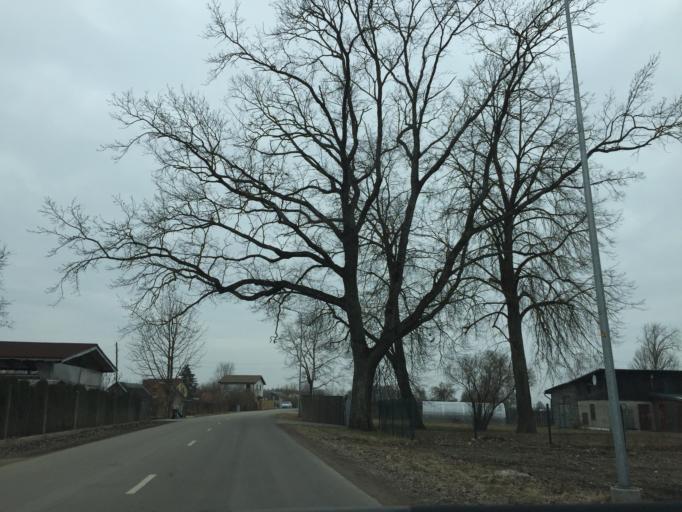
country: LV
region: Marupe
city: Marupe
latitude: 56.8781
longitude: 24.0656
